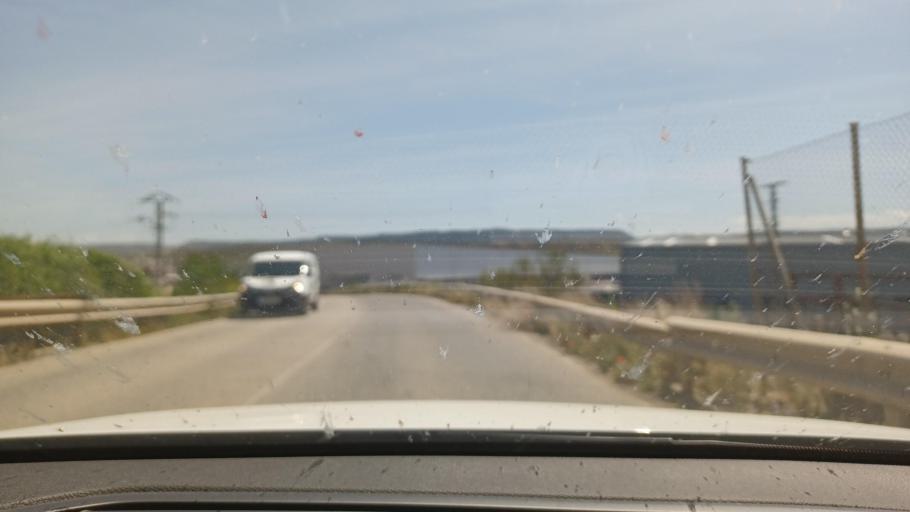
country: ES
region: Castille-La Mancha
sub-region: Provincia de Guadalajara
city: Alovera
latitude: 40.5933
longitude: -3.2327
